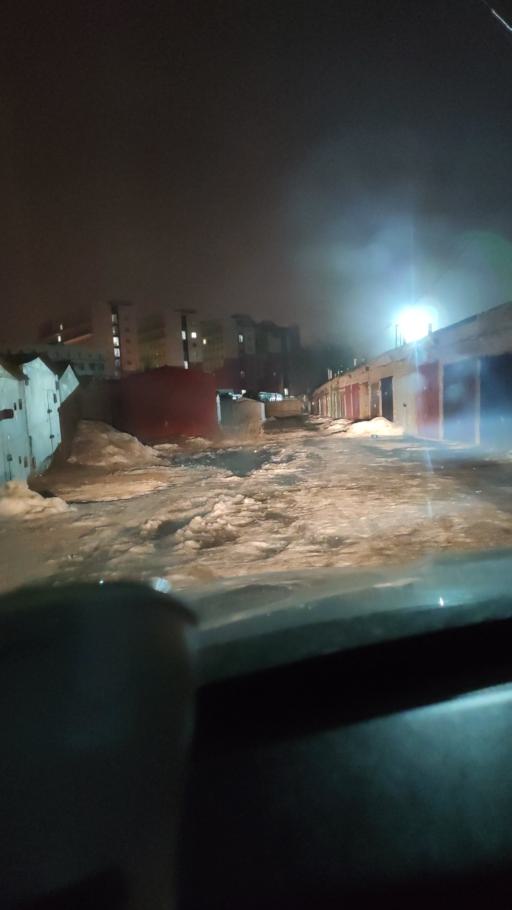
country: RU
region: Samara
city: Samara
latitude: 53.1849
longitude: 50.1113
